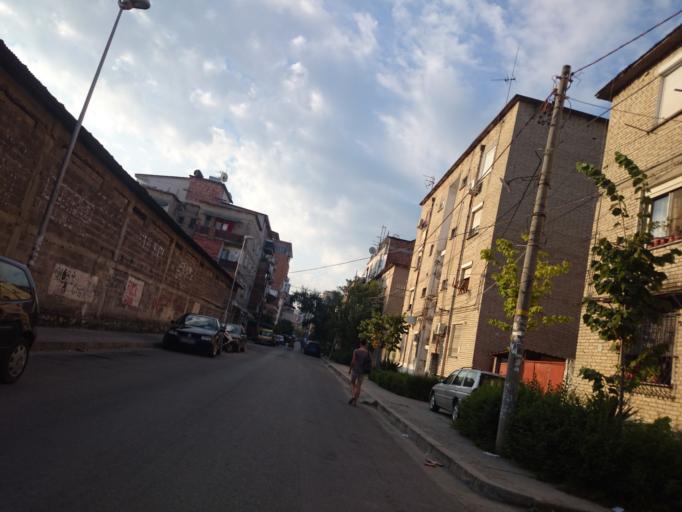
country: AL
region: Tirane
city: Tirana
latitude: 41.3271
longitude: 19.7934
